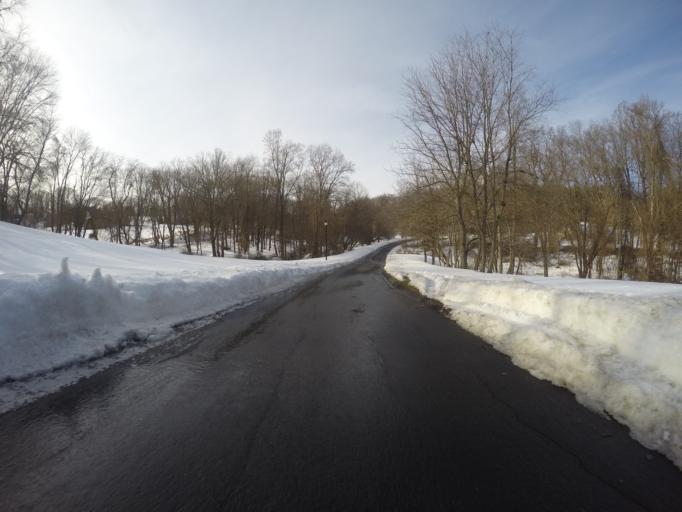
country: US
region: Maryland
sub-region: Baltimore County
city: Hunt Valley
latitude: 39.5644
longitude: -76.6444
